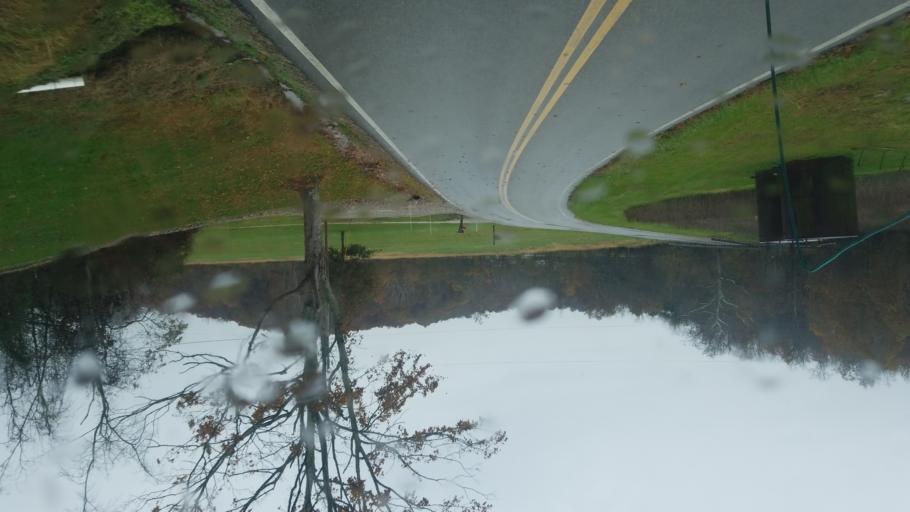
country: US
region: West Virginia
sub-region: Wood County
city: Blennerhassett
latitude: 39.3347
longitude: -81.6216
